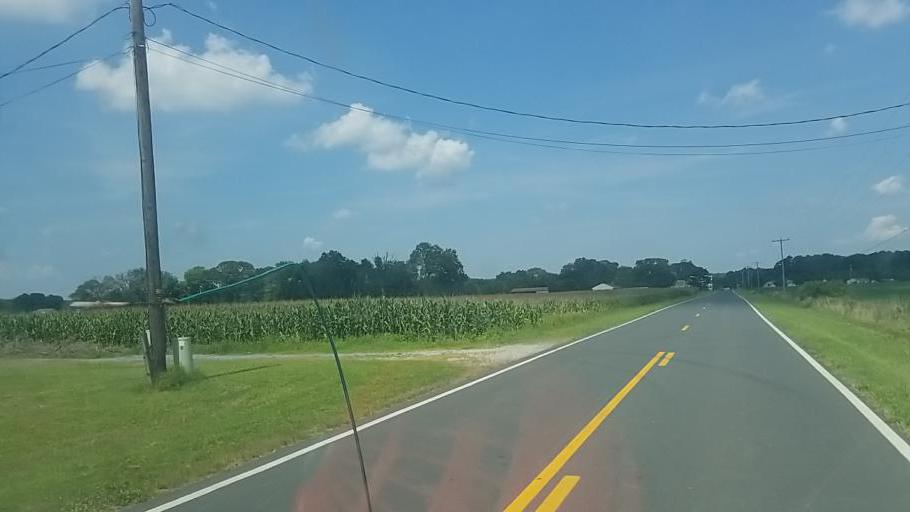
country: US
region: Maryland
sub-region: Wicomico County
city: Salisbury
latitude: 38.3496
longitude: -75.5225
